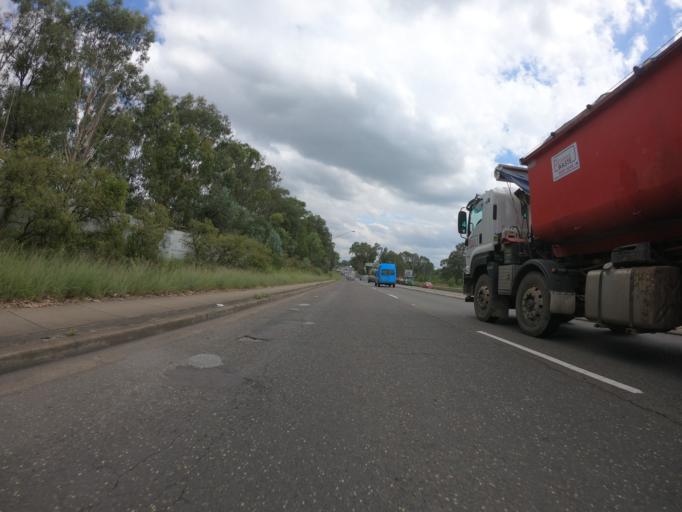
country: AU
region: New South Wales
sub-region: Blacktown
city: Mount Druitt
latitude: -33.7858
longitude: 150.7708
